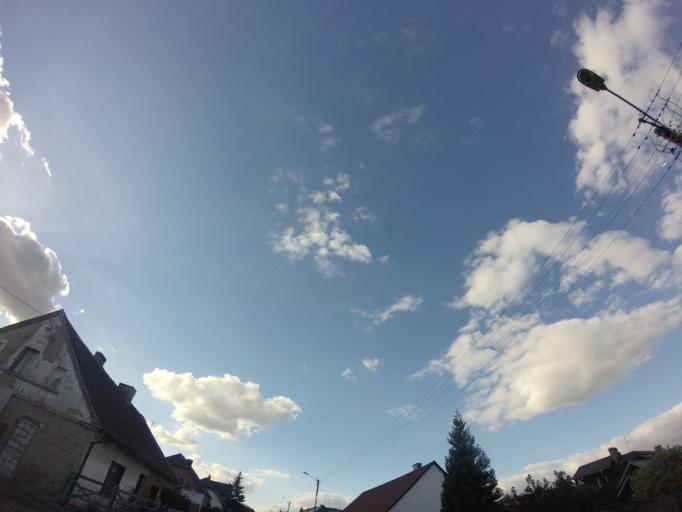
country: PL
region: Greater Poland Voivodeship
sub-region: Powiat nowotomyski
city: Nowy Tomysl
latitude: 52.2655
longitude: 16.1363
